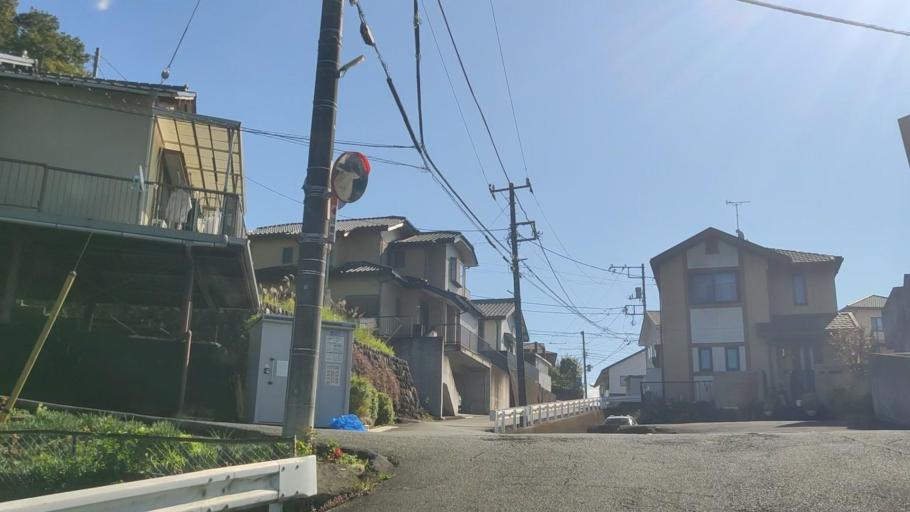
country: JP
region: Shizuoka
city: Ito
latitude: 34.9780
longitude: 138.9525
